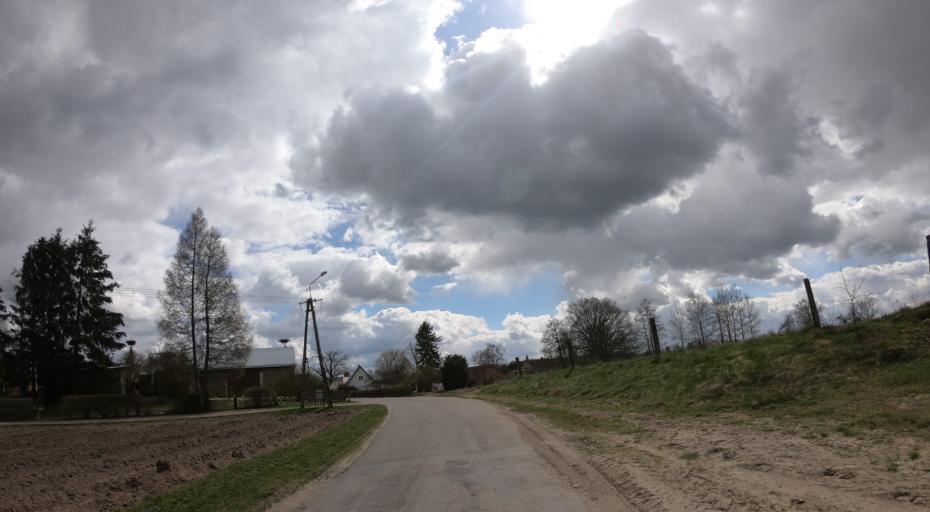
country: PL
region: West Pomeranian Voivodeship
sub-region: Powiat drawski
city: Drawsko Pomorskie
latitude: 53.5269
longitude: 15.8863
